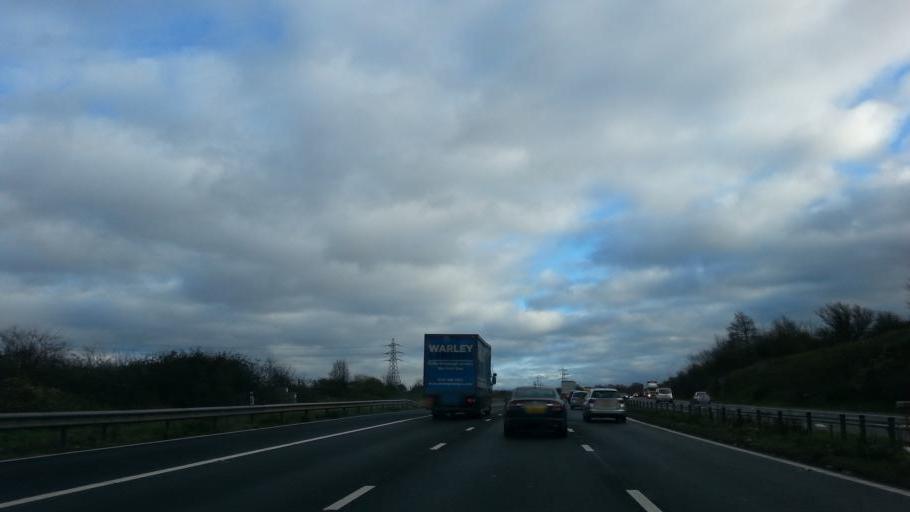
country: GB
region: England
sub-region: Wiltshire
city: Royal Wootton Bassett
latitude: 51.5592
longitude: -1.9028
